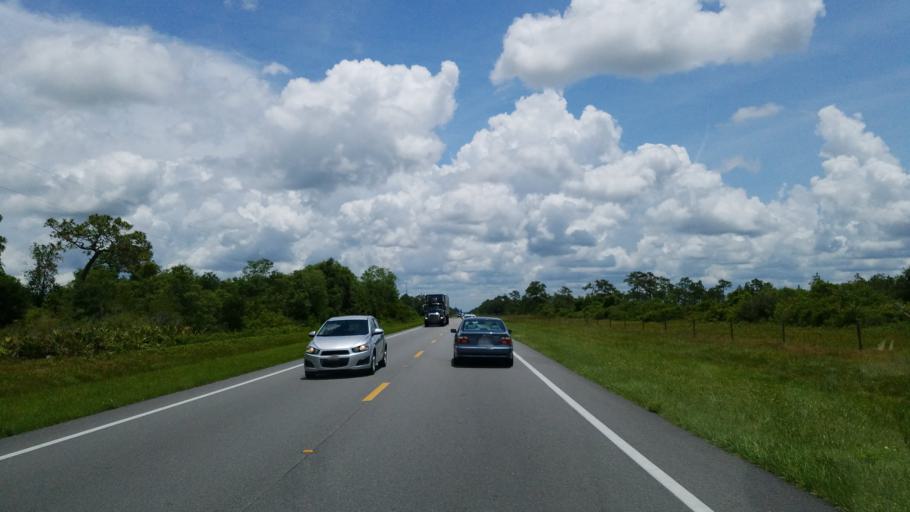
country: US
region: Florida
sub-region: Indian River County
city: Fellsmere
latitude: 27.7118
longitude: -80.9350
